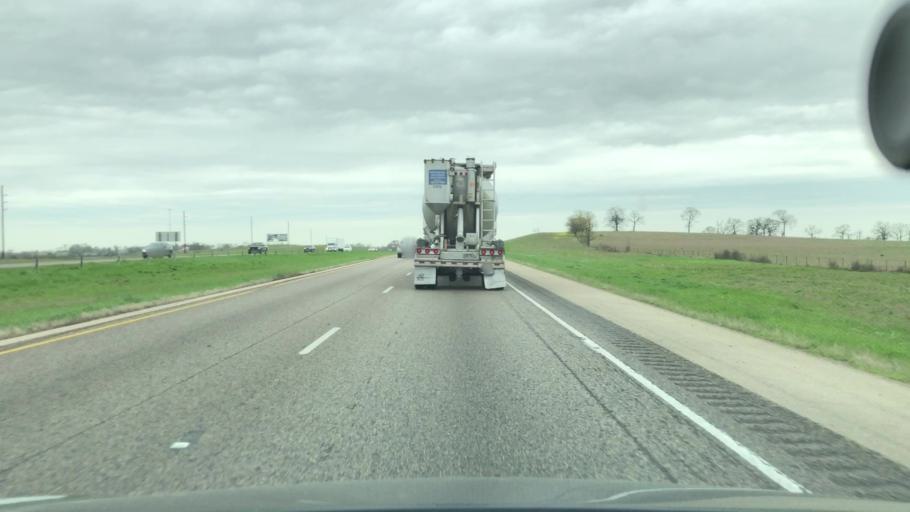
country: US
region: Texas
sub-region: Madison County
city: Madisonville
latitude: 31.0347
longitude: -95.9377
